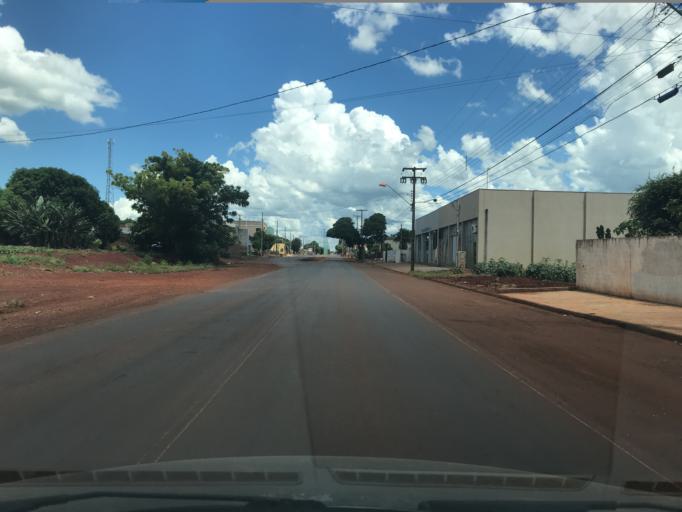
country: BR
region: Parana
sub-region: Palotina
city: Palotina
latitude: -24.2675
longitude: -53.8417
